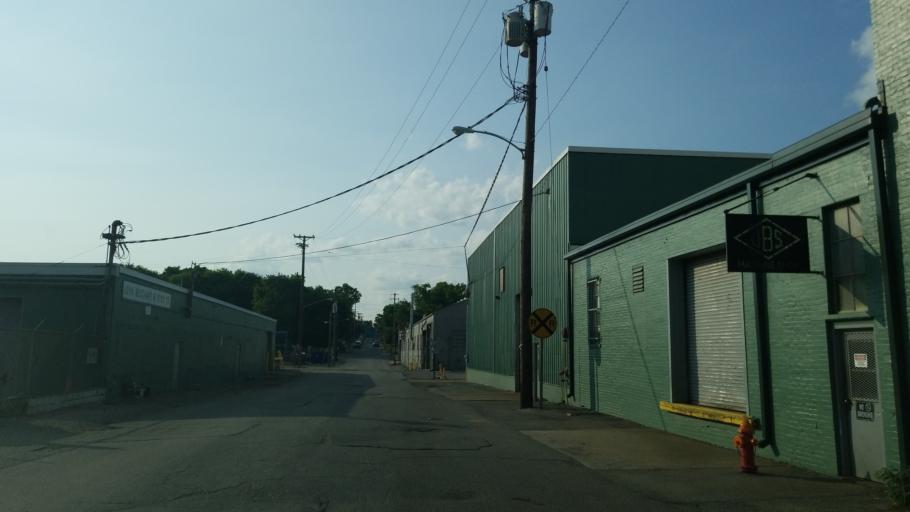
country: US
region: Tennessee
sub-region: Davidson County
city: Nashville
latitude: 36.1666
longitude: -86.7933
